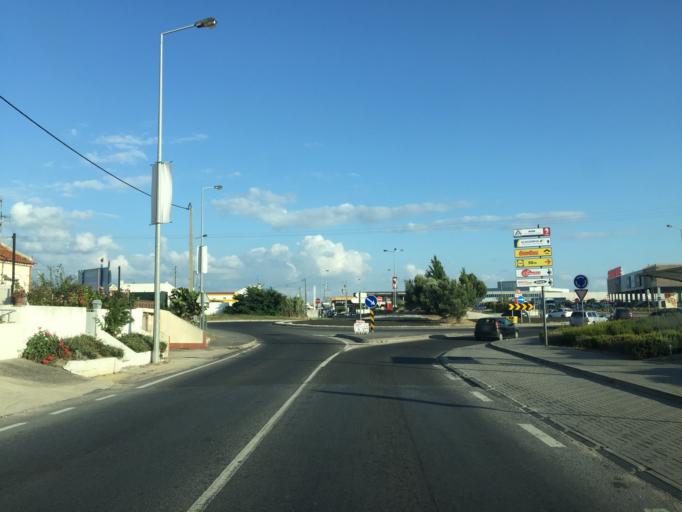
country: PT
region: Lisbon
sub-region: Alenquer
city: Carregado
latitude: 39.0411
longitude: -8.9871
